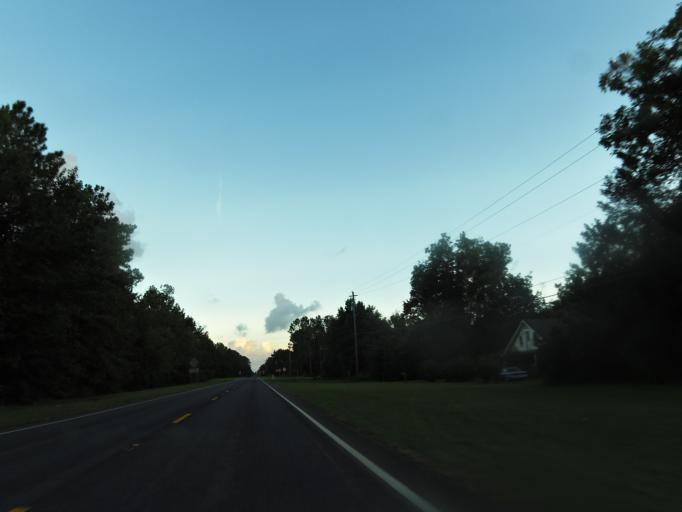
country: US
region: Georgia
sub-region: Camden County
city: Woodbine
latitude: 30.9381
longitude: -81.7177
